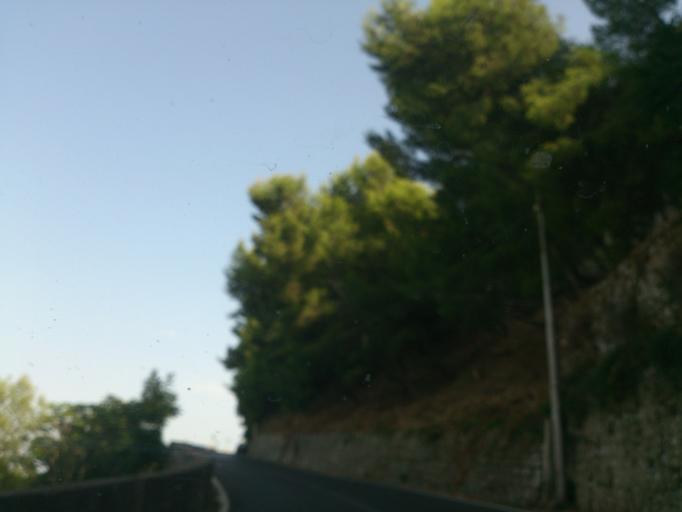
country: IT
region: Calabria
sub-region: Provincia di Reggio Calabria
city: Monasterace
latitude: 38.4541
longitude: 16.5527
